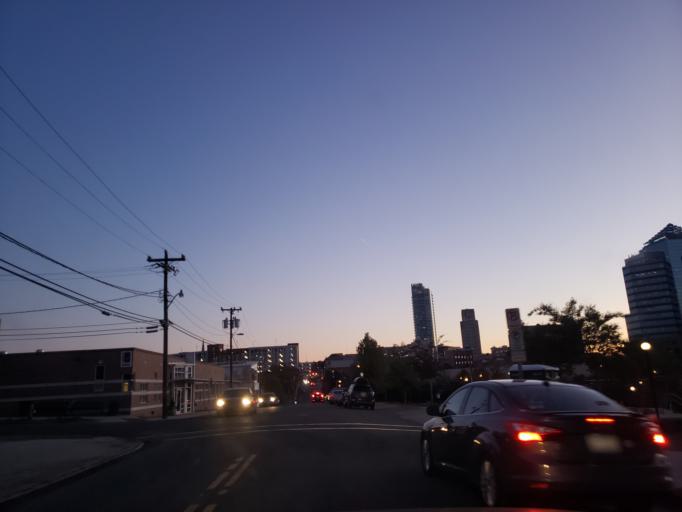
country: US
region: North Carolina
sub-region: Durham County
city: Durham
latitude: 36.0012
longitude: -78.9000
